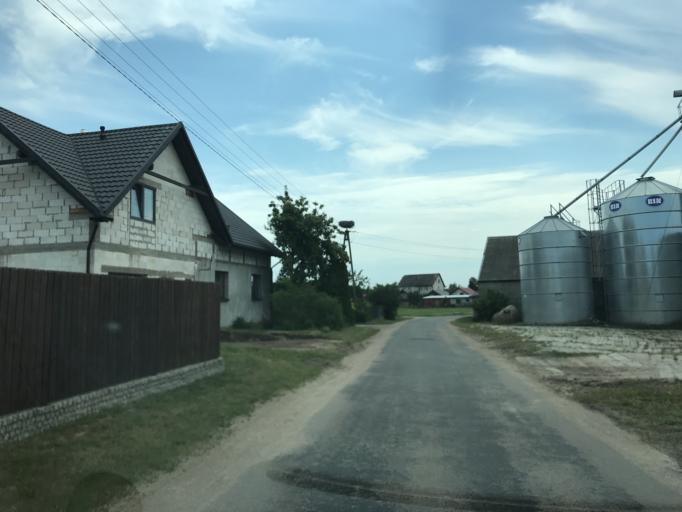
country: PL
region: Kujawsko-Pomorskie
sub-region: Powiat brodnicki
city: Bartniczka
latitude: 53.2515
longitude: 19.5666
